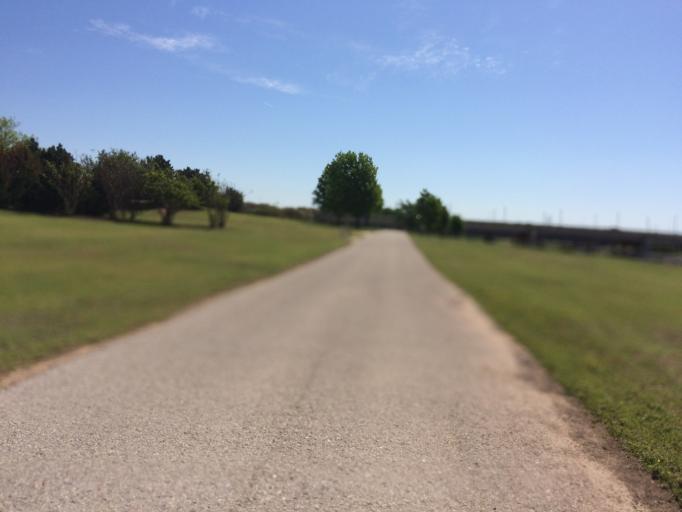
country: US
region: Oklahoma
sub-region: Oklahoma County
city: Oklahoma City
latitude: 35.4491
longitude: -97.5182
